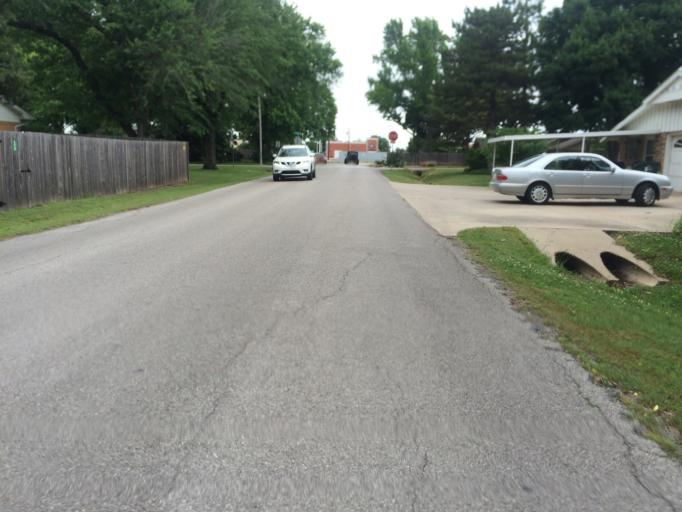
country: US
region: Oklahoma
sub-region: Cleveland County
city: Norman
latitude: 35.2160
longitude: -97.4806
